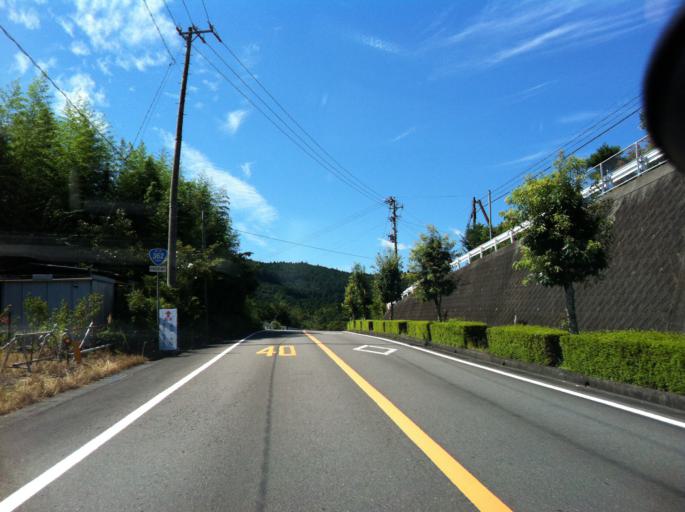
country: JP
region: Shizuoka
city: Fujieda
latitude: 35.0916
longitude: 138.1265
